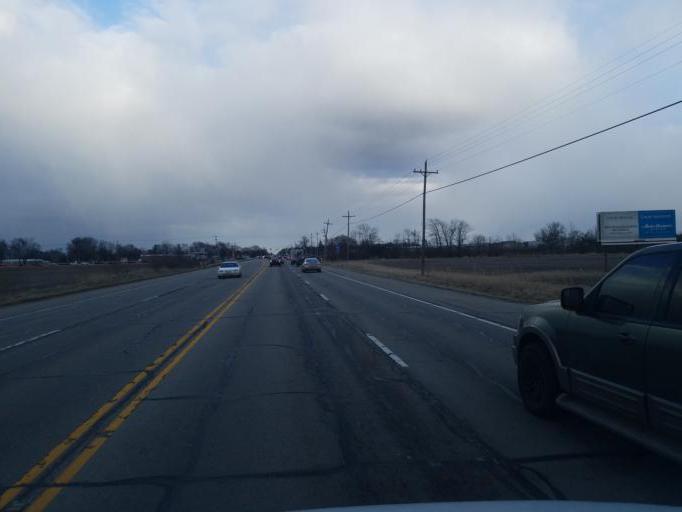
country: US
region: Indiana
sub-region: Marion County
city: Cumberland
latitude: 39.7784
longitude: -85.9185
